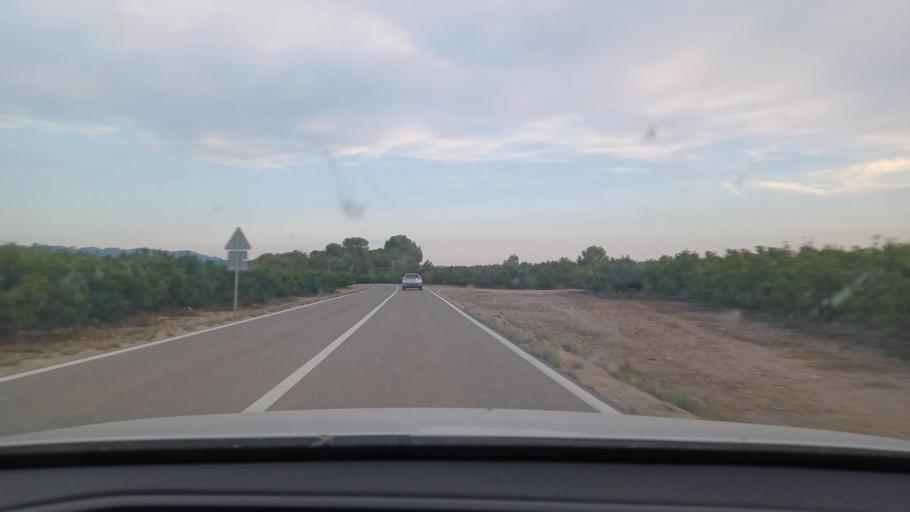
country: ES
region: Catalonia
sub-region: Provincia de Tarragona
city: Santa Barbara
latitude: 40.7184
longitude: 0.4675
